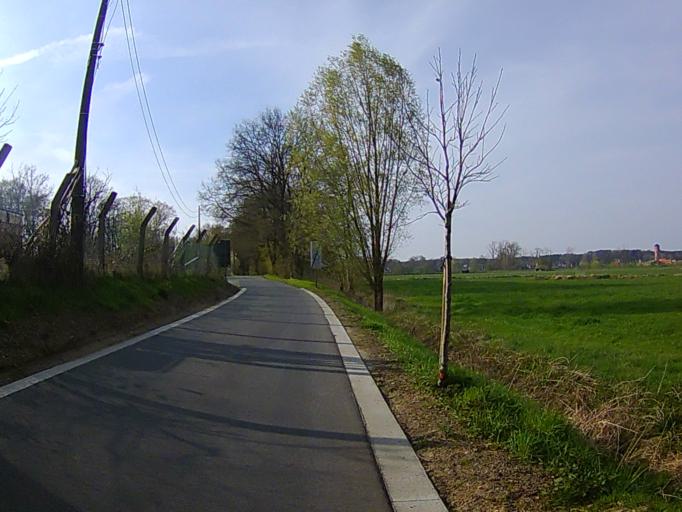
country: BE
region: Flanders
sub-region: Provincie Antwerpen
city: Grobbendonk
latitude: 51.1874
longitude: 4.7502
